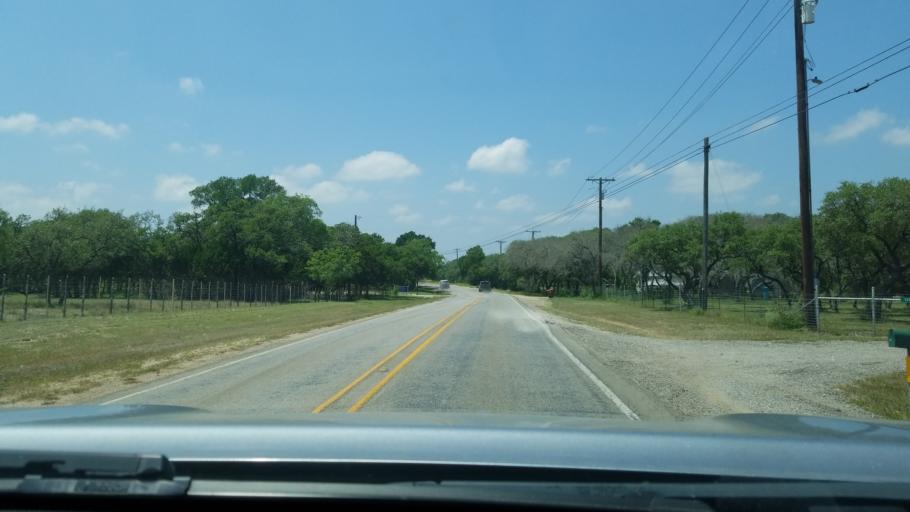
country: US
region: Texas
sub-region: Hays County
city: Woodcreek
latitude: 30.0322
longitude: -98.1729
